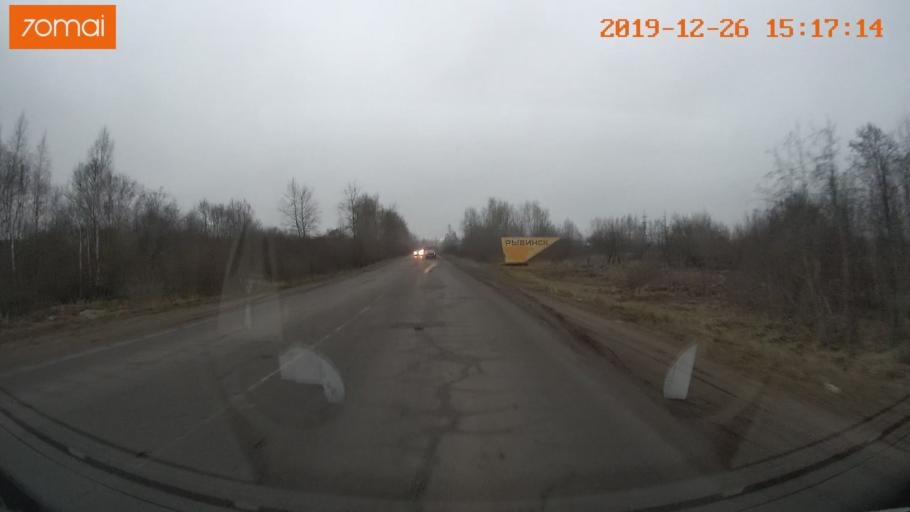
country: RU
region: Jaroslavl
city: Rybinsk
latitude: 58.0790
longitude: 38.8527
